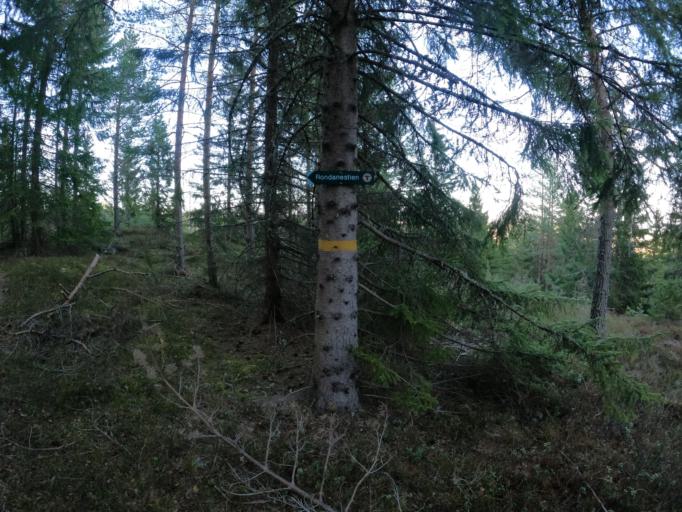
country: NO
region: Akershus
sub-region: Nannestad
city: Teigebyen
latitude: 60.2360
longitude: 10.9696
